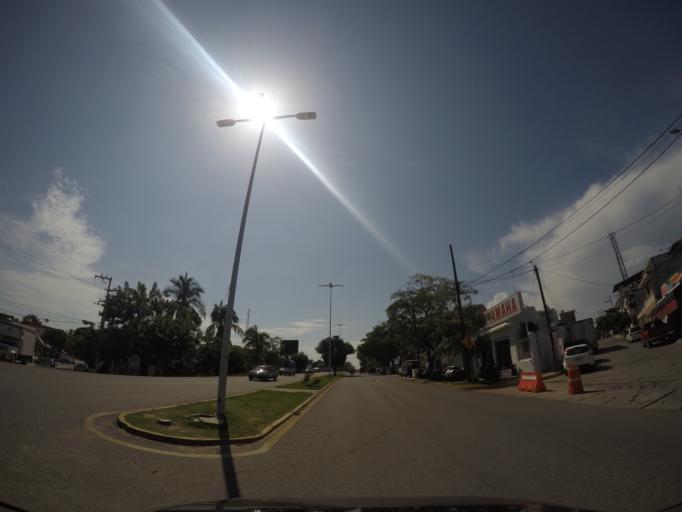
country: MX
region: Oaxaca
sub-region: San Pedro Mixtepec -Dto. 22 -
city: Puerto Escondido
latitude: 15.8624
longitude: -97.0700
